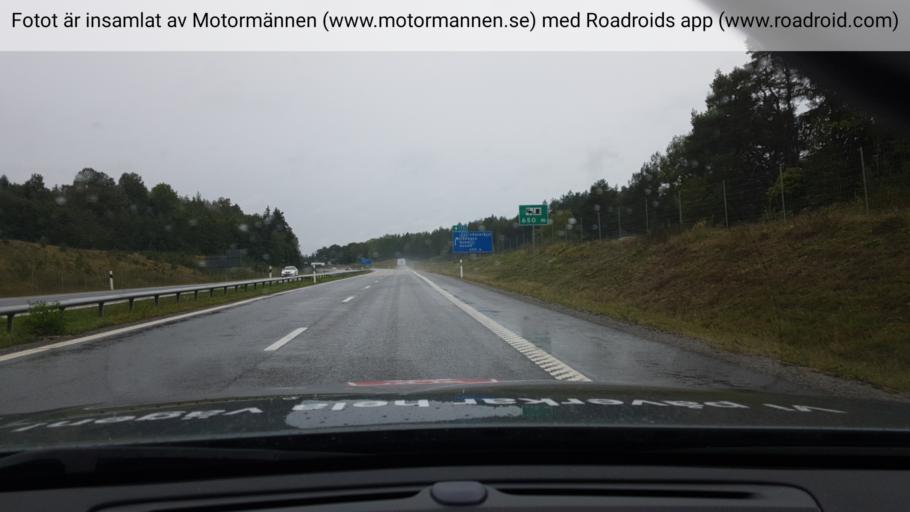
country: SE
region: Stockholm
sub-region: Nynashamns Kommun
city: Osmo
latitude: 58.9877
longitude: 17.9230
